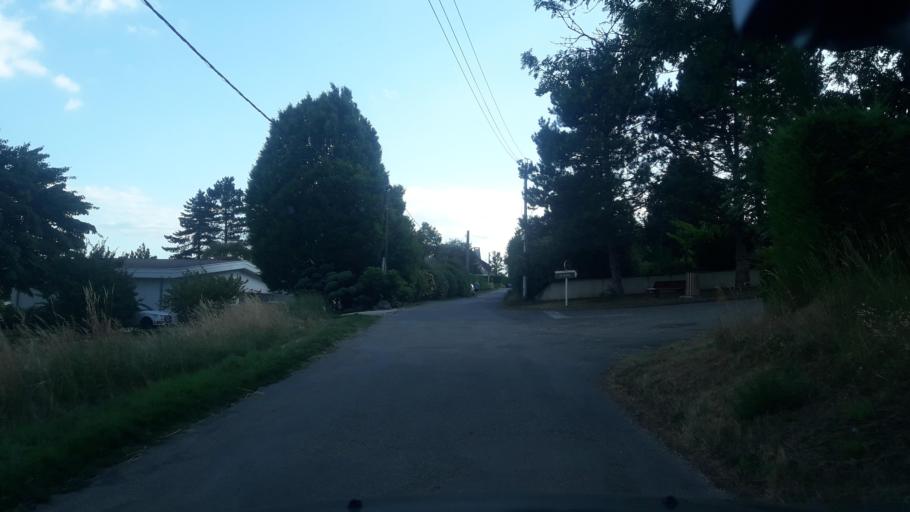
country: FR
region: Rhone-Alpes
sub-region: Departement de l'Isere
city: Saint-Ismier
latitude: 45.2431
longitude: 5.8140
